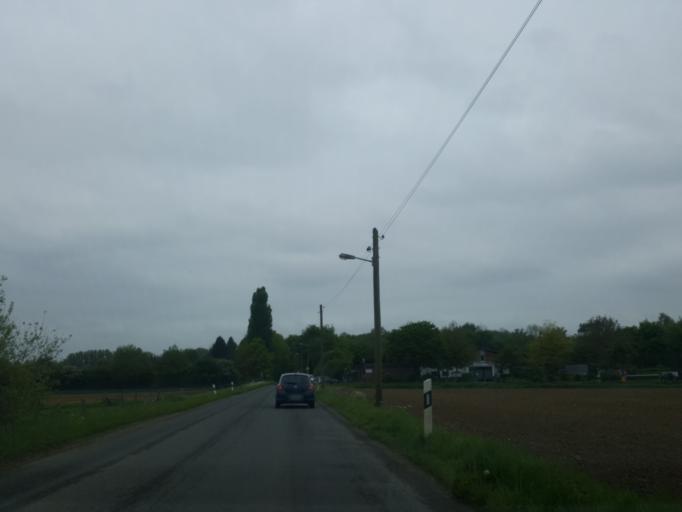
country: DE
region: North Rhine-Westphalia
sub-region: Regierungsbezirk Dusseldorf
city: Krefeld
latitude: 51.3650
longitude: 6.5601
